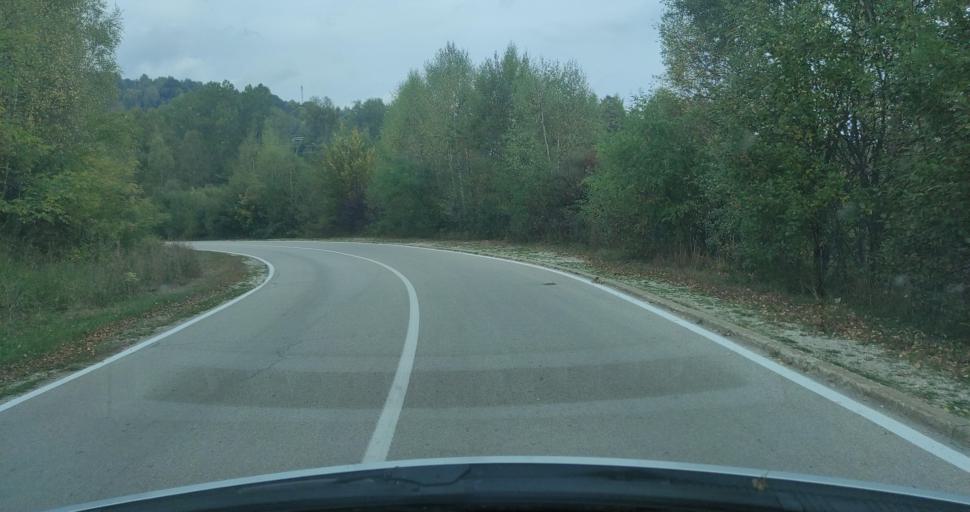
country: RS
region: Central Serbia
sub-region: Jablanicki Okrug
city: Crna Trava
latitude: 42.7378
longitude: 22.3304
